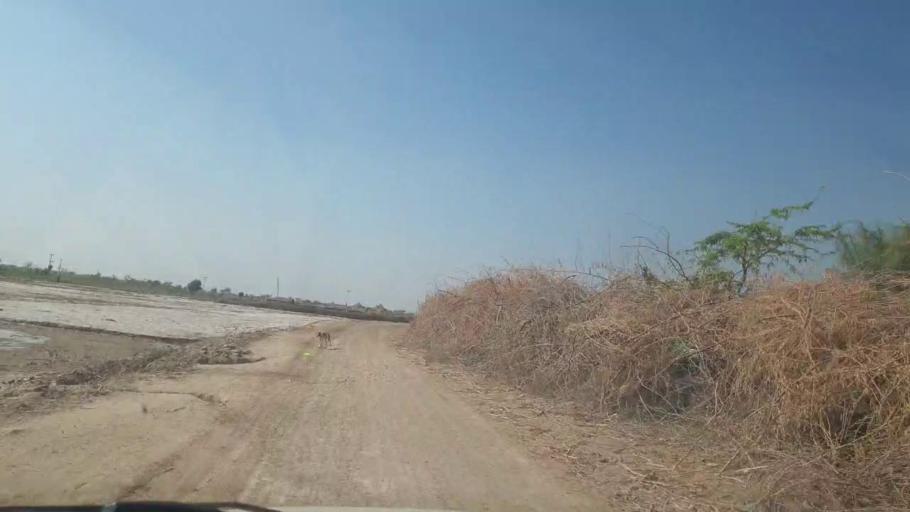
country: PK
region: Sindh
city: Mirpur Khas
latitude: 25.4743
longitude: 69.1231
